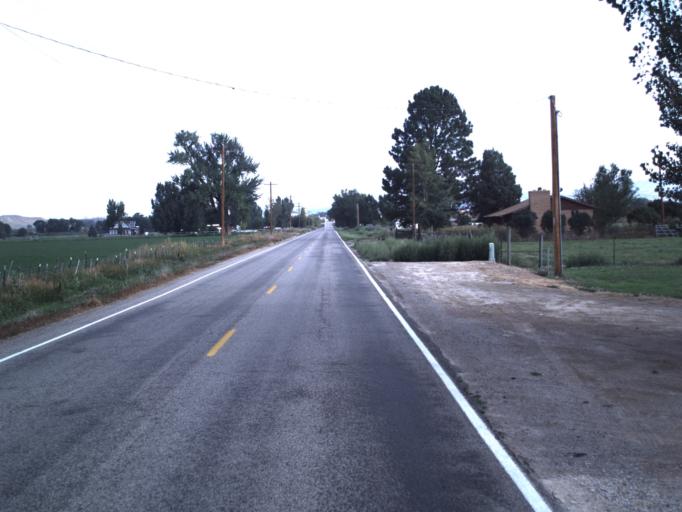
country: US
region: Utah
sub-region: Uintah County
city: Naples
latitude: 40.3787
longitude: -109.3458
